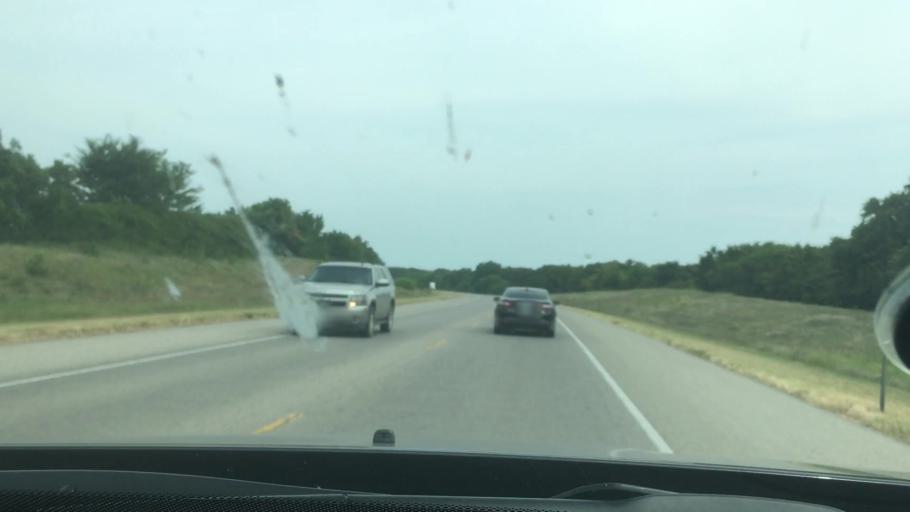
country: US
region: Oklahoma
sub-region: Pontotoc County
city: Ada
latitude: 34.6985
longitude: -96.5999
